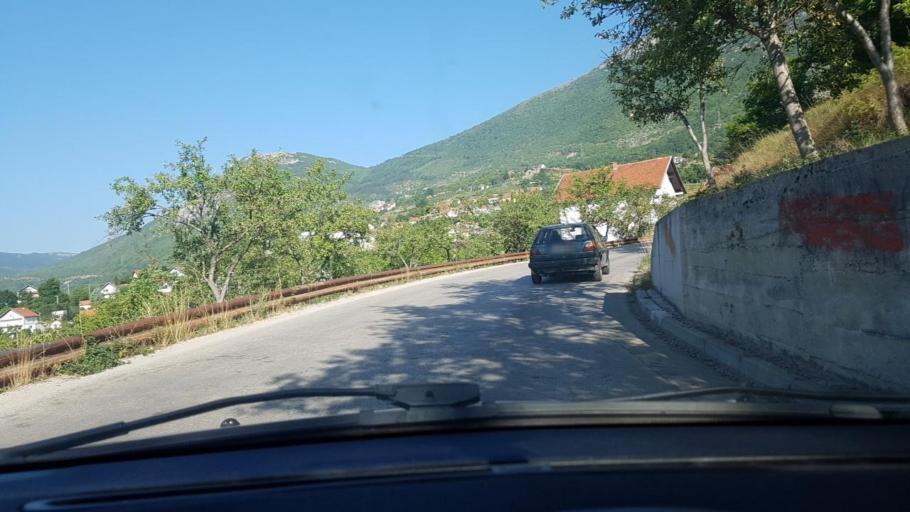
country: BA
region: Federation of Bosnia and Herzegovina
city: Rumboci
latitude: 43.8286
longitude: 17.5125
